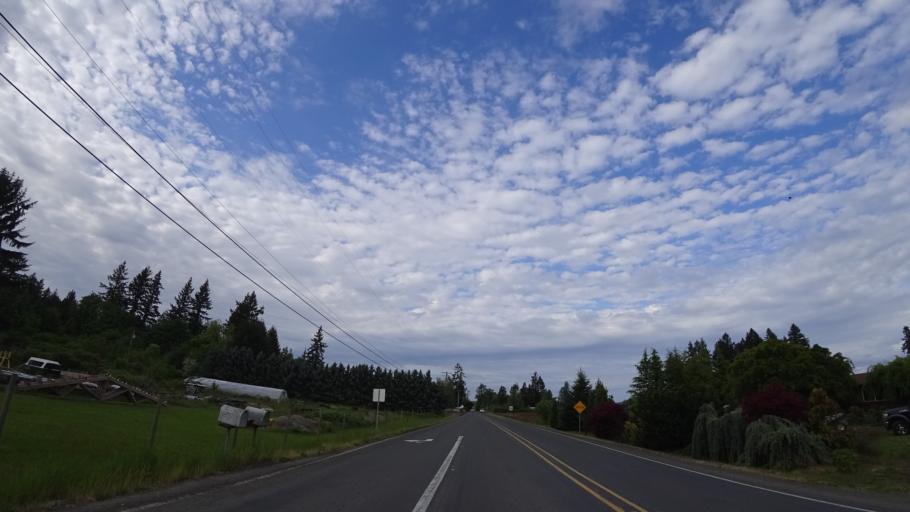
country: US
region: Oregon
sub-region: Washington County
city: Hillsboro
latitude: 45.4802
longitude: -122.9854
